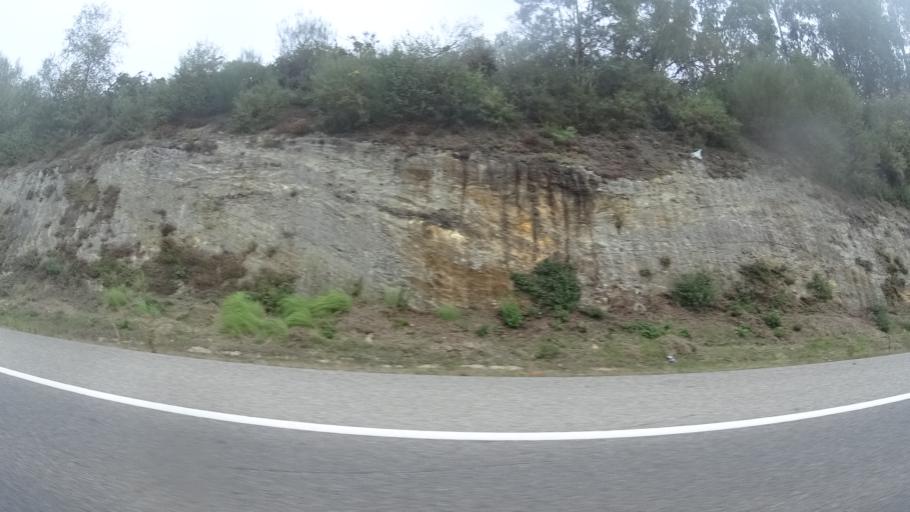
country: ES
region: Galicia
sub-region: Provincia de Lugo
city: Guitiriz
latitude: 43.1926
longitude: -7.8724
